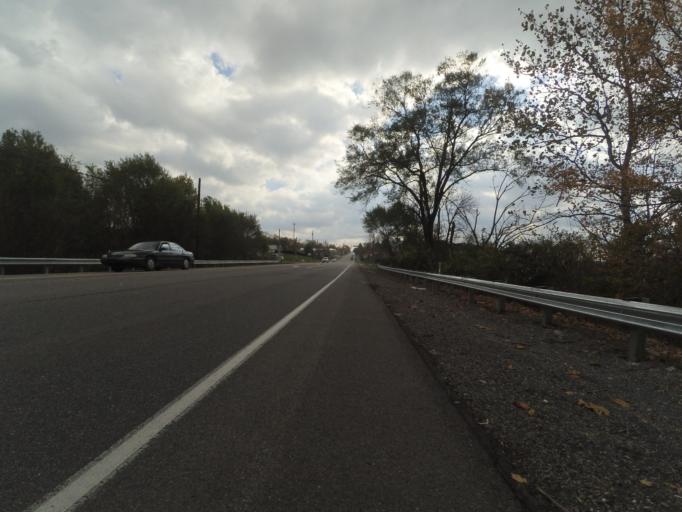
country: US
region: Pennsylvania
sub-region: Centre County
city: Bellefonte
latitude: 40.8966
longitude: -77.7879
